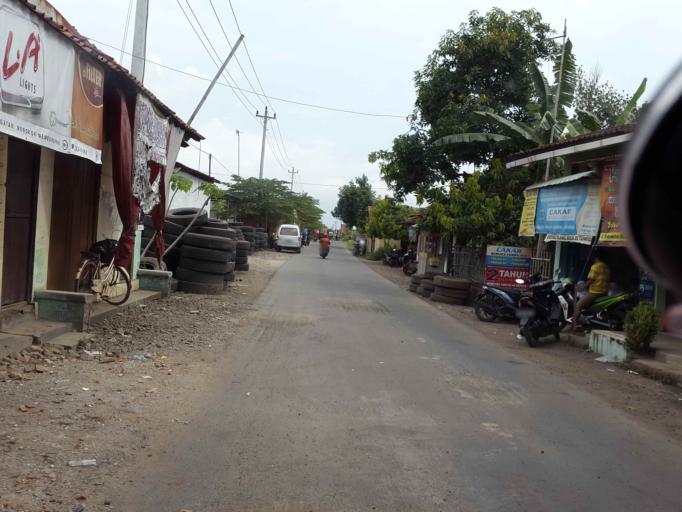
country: ID
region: Central Java
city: Comal
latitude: -6.8862
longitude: 109.5543
